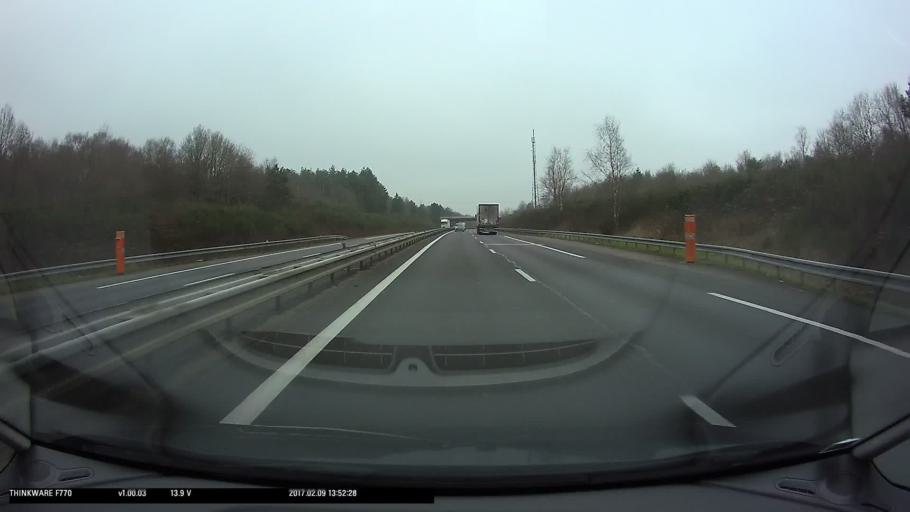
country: FR
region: Centre
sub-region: Departement du Loiret
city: La Ferte-Saint-Aubin
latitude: 47.7057
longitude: 1.9020
